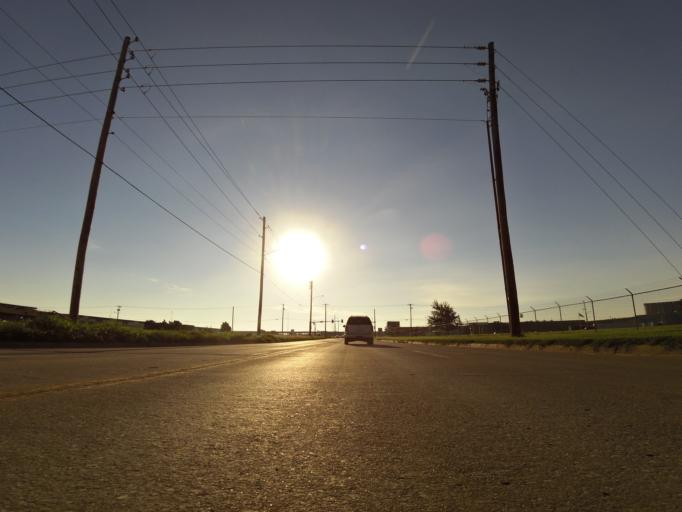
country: US
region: Kansas
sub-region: Sedgwick County
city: Wichita
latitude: 37.7375
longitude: -97.3259
